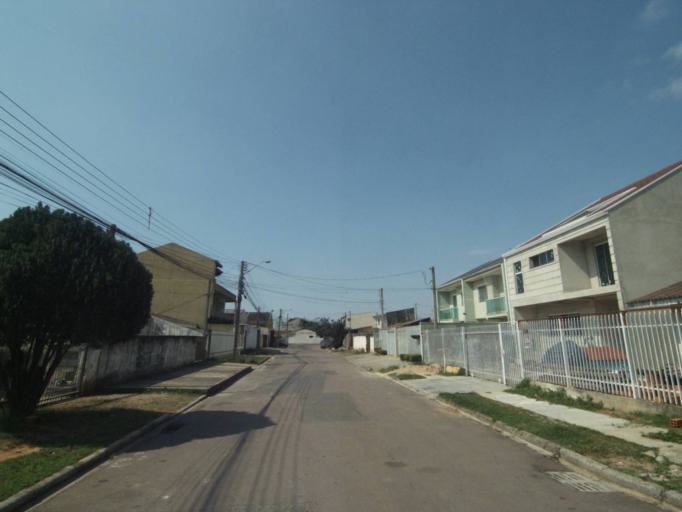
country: BR
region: Parana
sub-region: Curitiba
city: Curitiba
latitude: -25.4893
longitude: -49.3349
